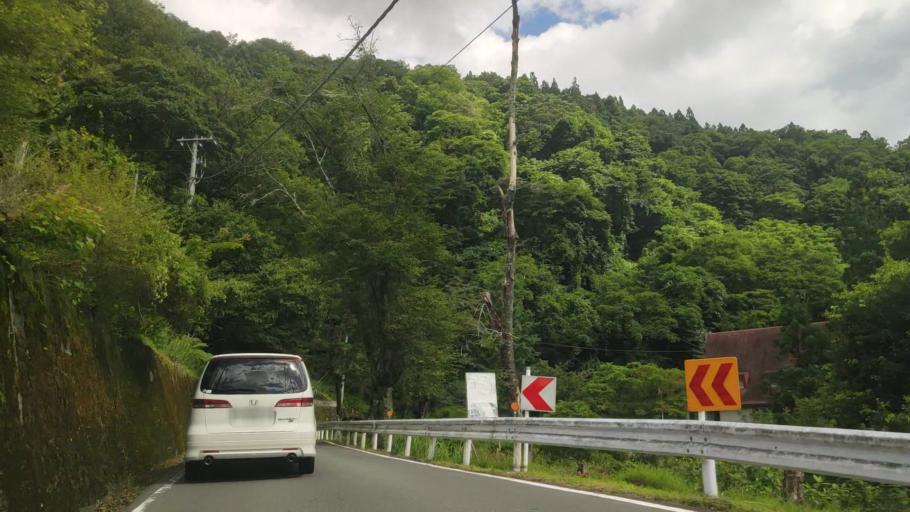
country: JP
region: Saitama
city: Chichibu
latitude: 35.9370
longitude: 138.9079
